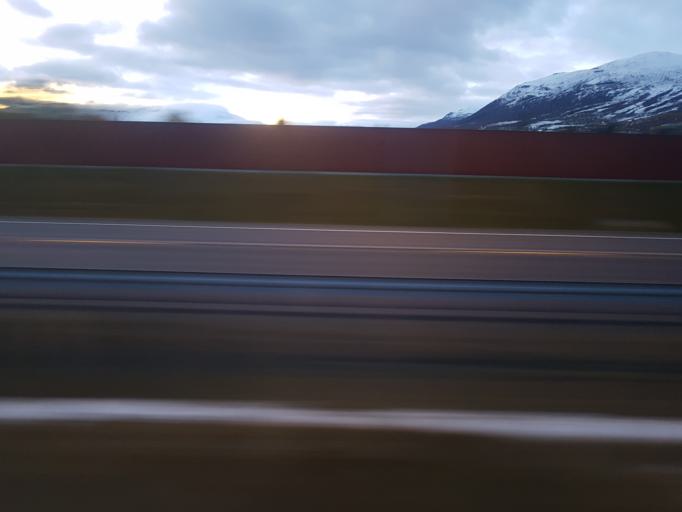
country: NO
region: Sor-Trondelag
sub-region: Oppdal
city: Oppdal
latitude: 62.5855
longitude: 9.6628
